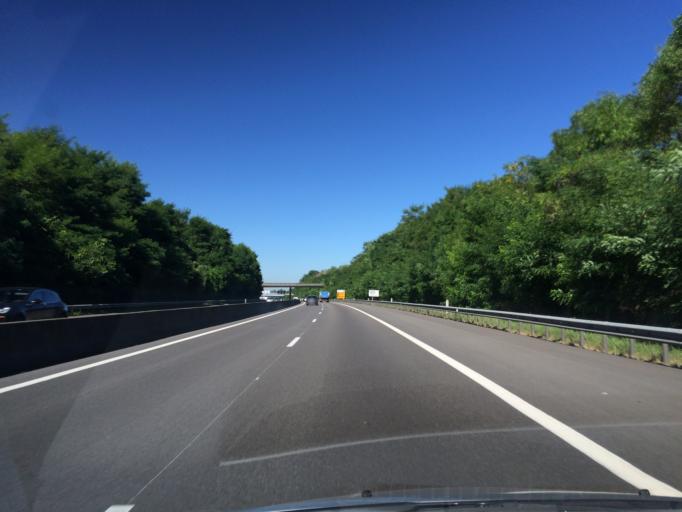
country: LU
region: Luxembourg
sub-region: Canton de Capellen
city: Mamer
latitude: 49.6368
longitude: 6.0243
